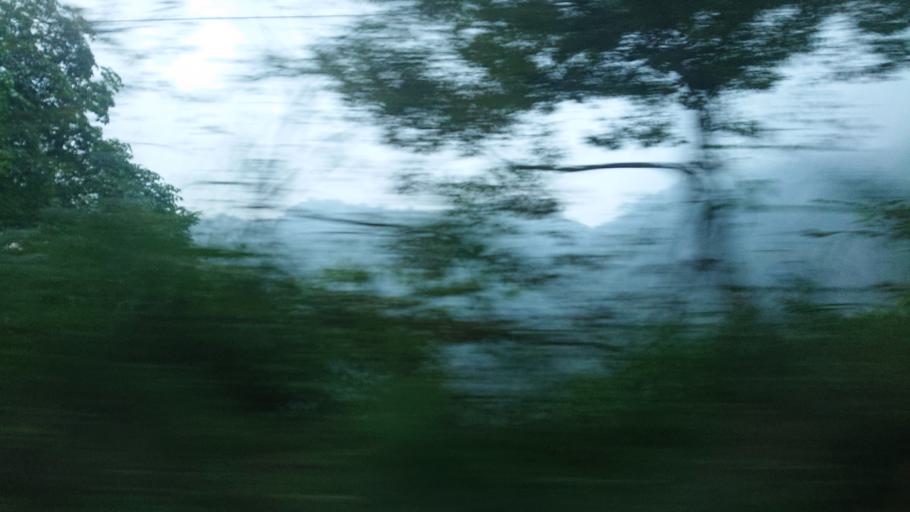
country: TW
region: Taiwan
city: Lugu
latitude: 23.5943
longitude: 120.7240
